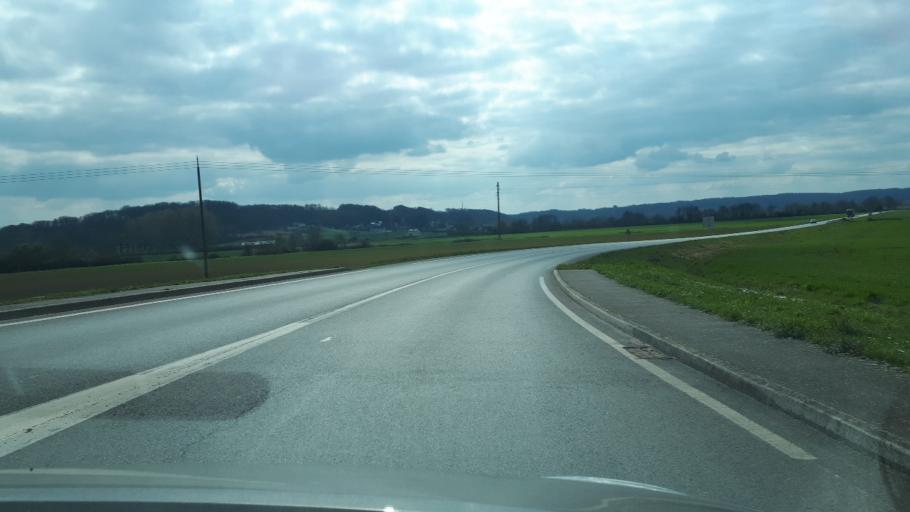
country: FR
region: Centre
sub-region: Departement du Loir-et-Cher
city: Lunay
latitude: 47.7699
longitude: 0.9108
